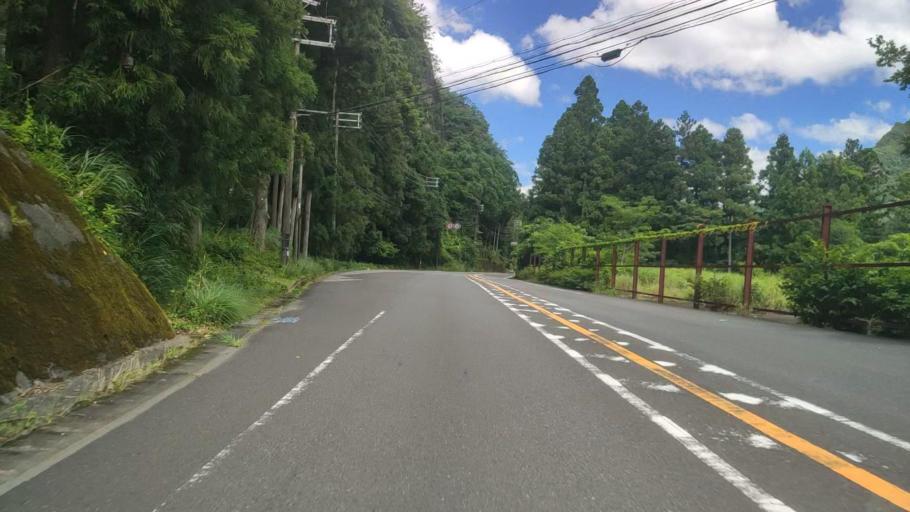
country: JP
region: Wakayama
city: Shingu
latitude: 33.7941
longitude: 135.8952
